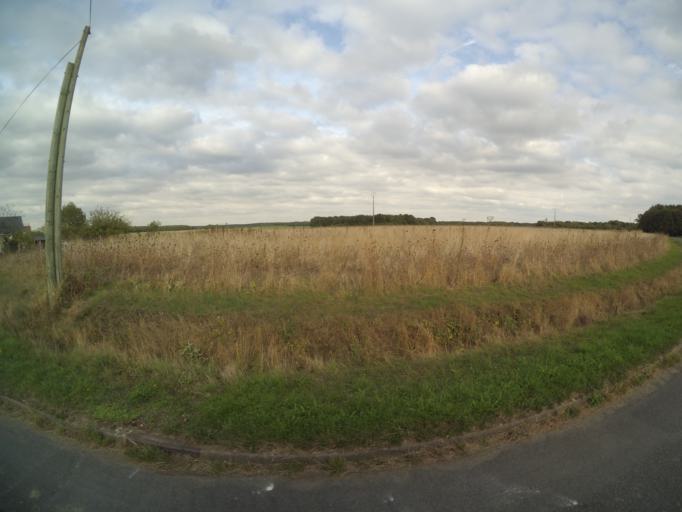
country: FR
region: Centre
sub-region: Departement d'Indre-et-Loire
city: Poce-sur-Cisse
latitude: 47.4722
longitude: 0.9681
